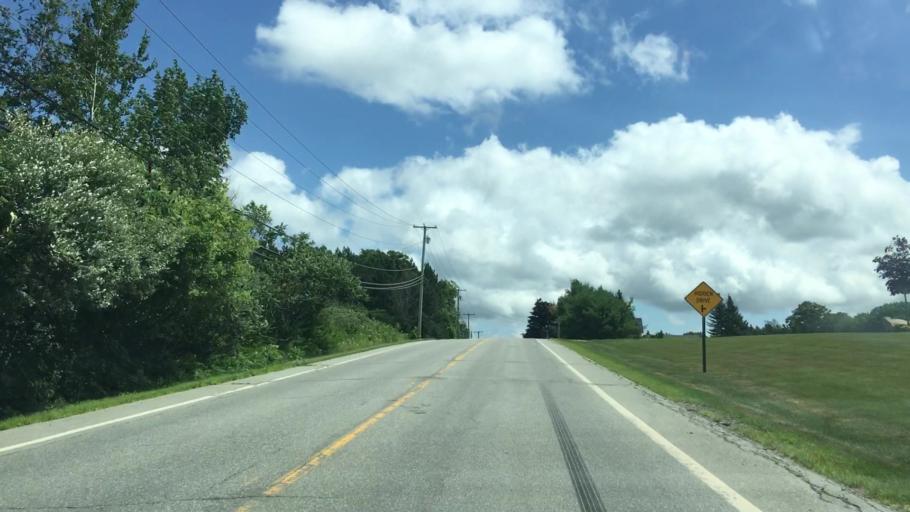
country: US
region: Maine
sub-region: Penobscot County
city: Carmel
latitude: 44.8031
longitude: -69.0293
